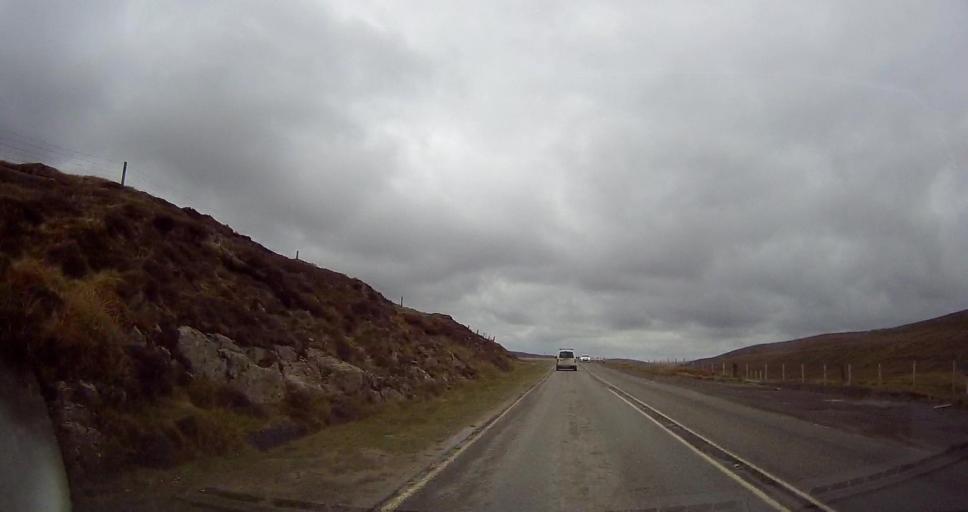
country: GB
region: Scotland
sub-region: Shetland Islands
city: Lerwick
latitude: 60.3243
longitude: -1.2522
